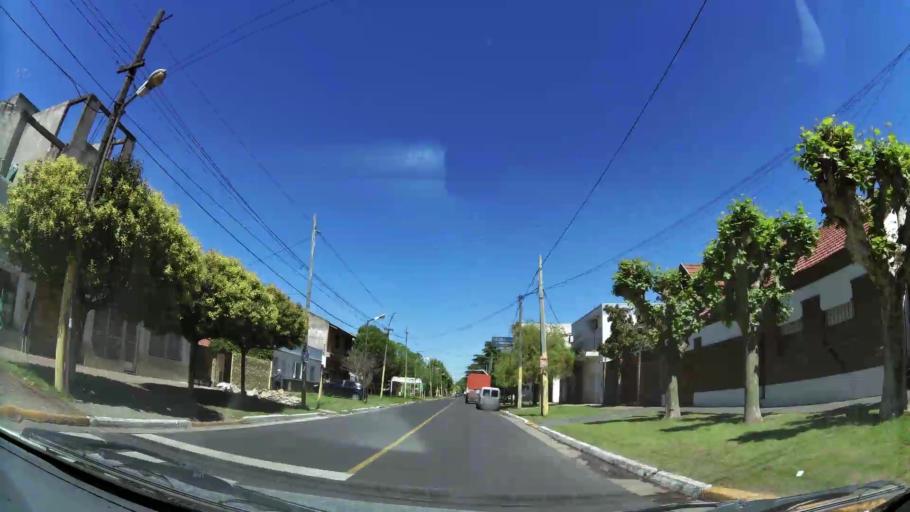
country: AR
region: Buenos Aires
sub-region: Partido de Quilmes
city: Quilmes
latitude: -34.7233
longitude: -58.2791
